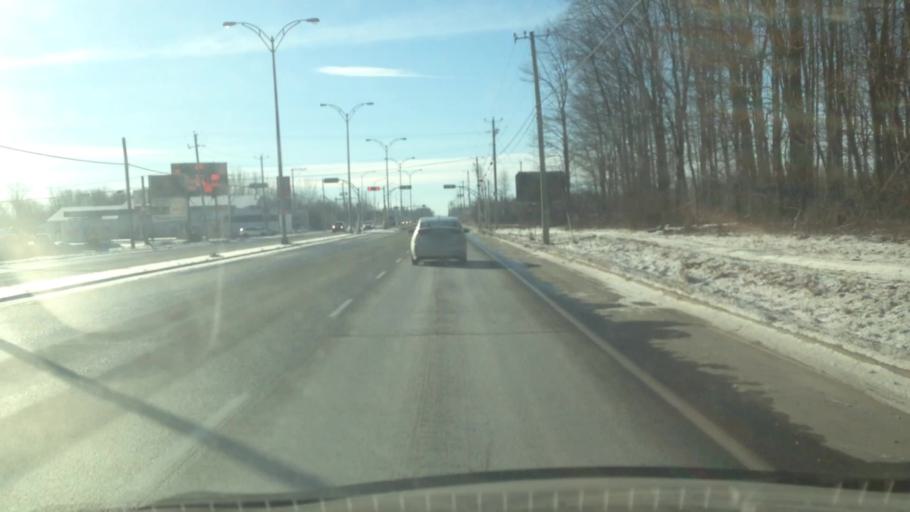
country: CA
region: Quebec
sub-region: Monteregie
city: Chateauguay
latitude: 45.3943
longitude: -73.6952
